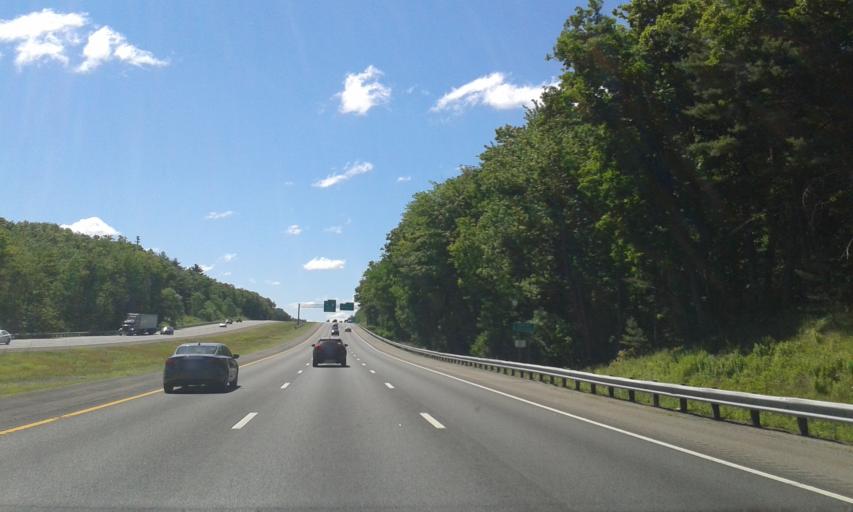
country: US
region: Massachusetts
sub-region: Middlesex County
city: Pinehurst
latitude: 42.4962
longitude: -71.2377
